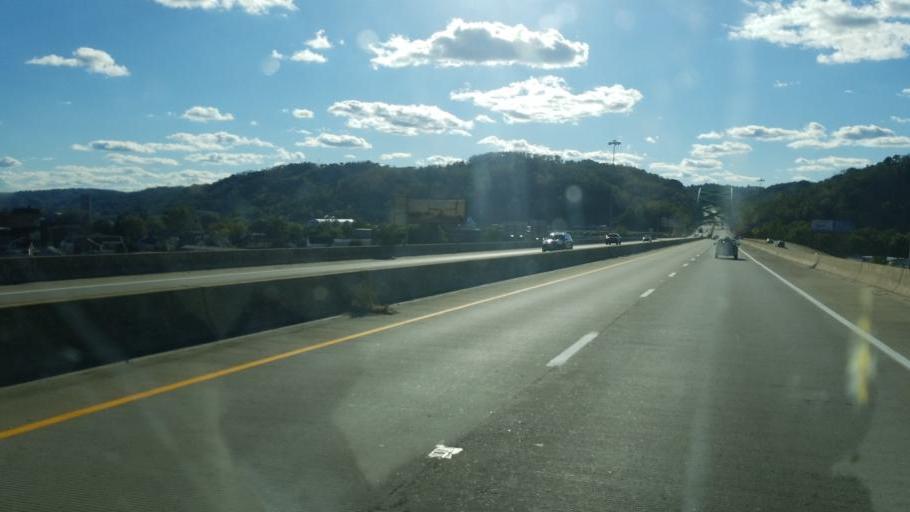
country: US
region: West Virginia
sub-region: Ohio County
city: Wheeling
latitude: 40.0512
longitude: -80.7218
